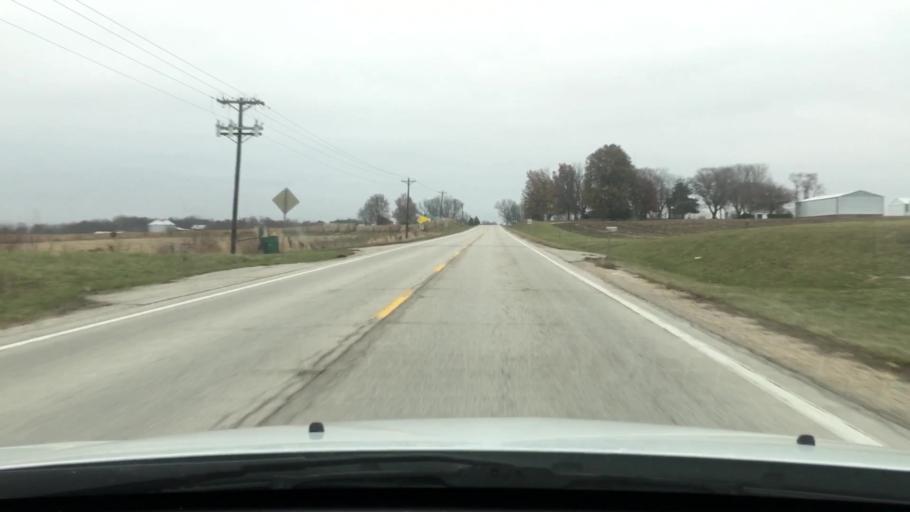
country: US
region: Illinois
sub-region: Pike County
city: Pittsfield
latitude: 39.5508
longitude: -90.9165
